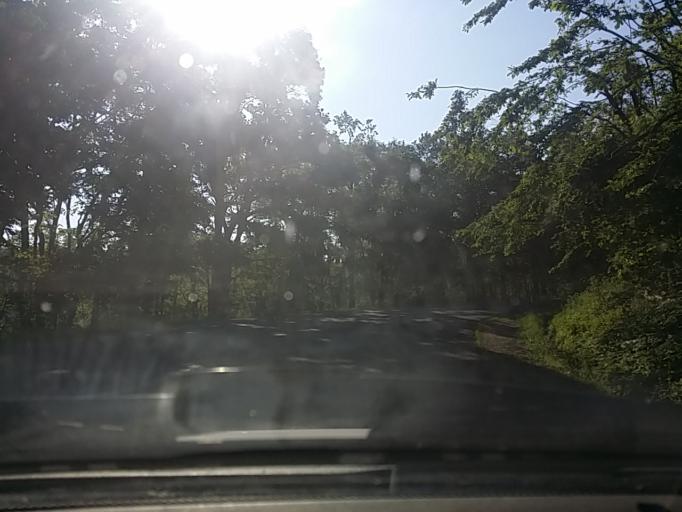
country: HU
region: Pest
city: Pilisszentkereszt
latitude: 47.7195
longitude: 18.8789
